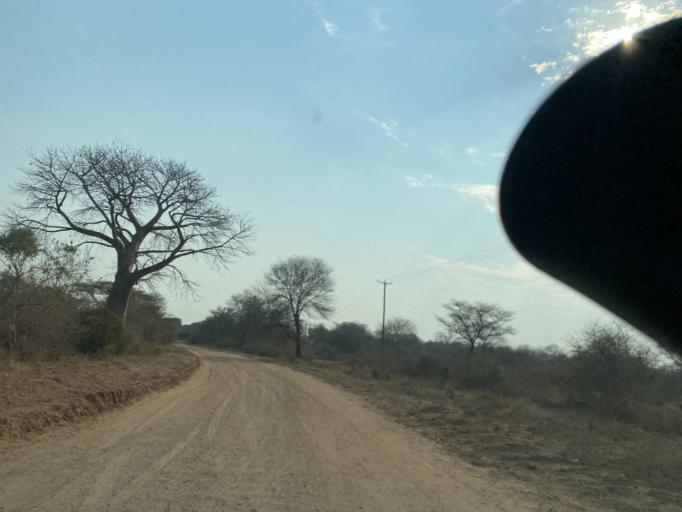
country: ZW
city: Chirundu
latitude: -15.9349
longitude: 28.9359
